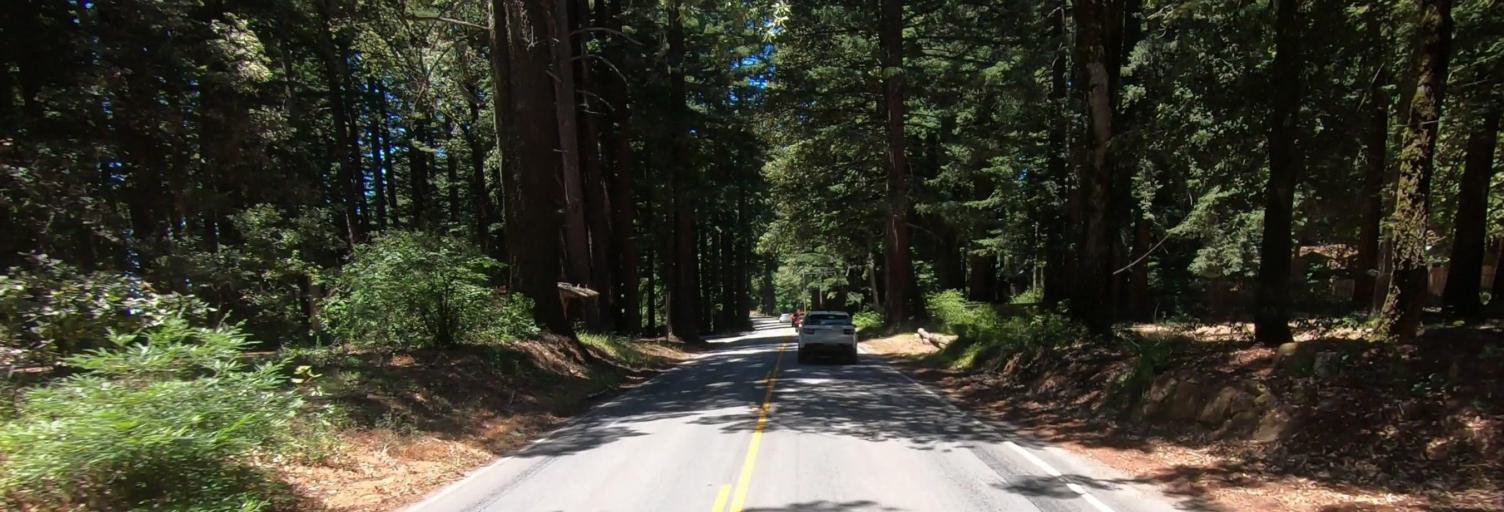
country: US
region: California
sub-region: San Mateo County
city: Emerald Lake Hills
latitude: 37.4434
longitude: -122.3299
